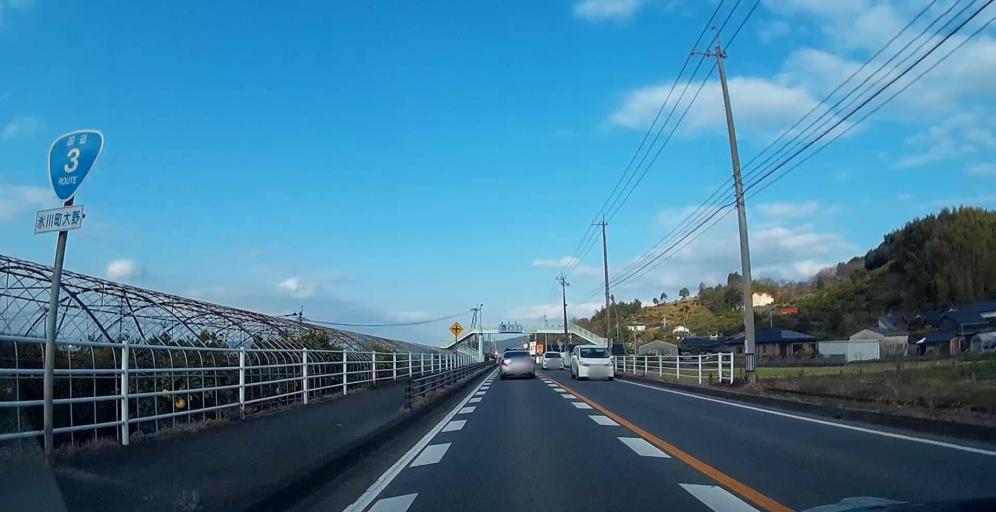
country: JP
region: Kumamoto
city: Matsubase
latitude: 32.5729
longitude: 130.6927
